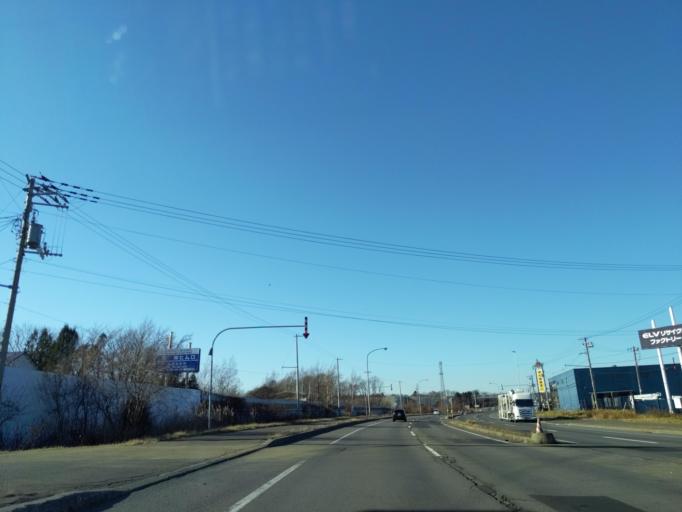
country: JP
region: Hokkaido
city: Kitahiroshima
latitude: 42.9360
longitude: 141.5148
